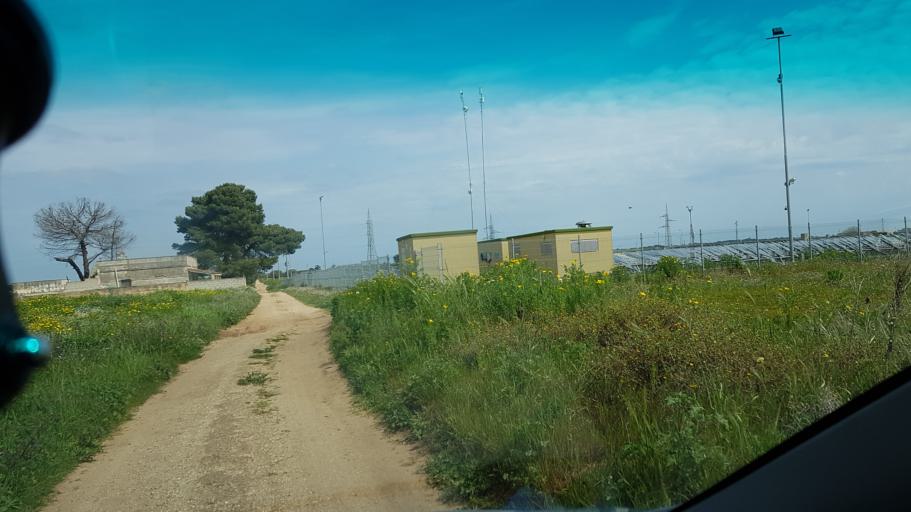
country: IT
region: Apulia
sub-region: Provincia di Brindisi
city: Mesagne
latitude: 40.6118
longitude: 17.8533
